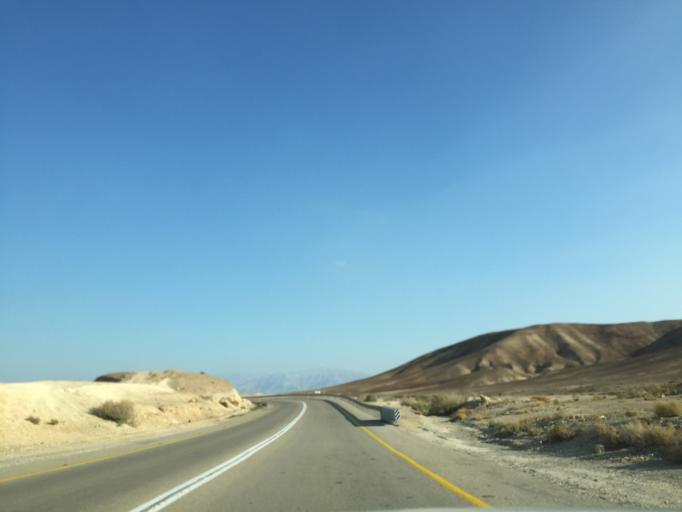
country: IL
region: Southern District
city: `En Boqeq
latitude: 31.1741
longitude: 35.3060
